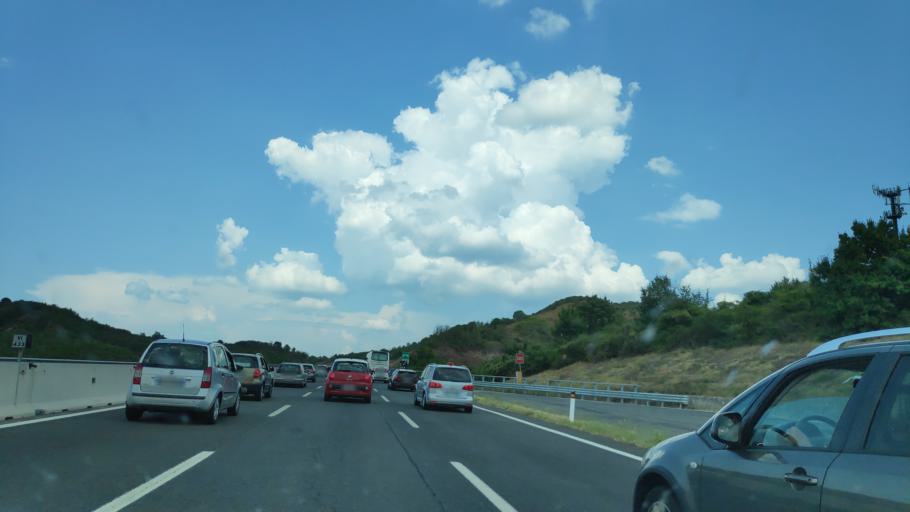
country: IT
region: Umbria
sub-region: Provincia di Terni
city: Ficulle
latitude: 42.8303
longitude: 12.0427
